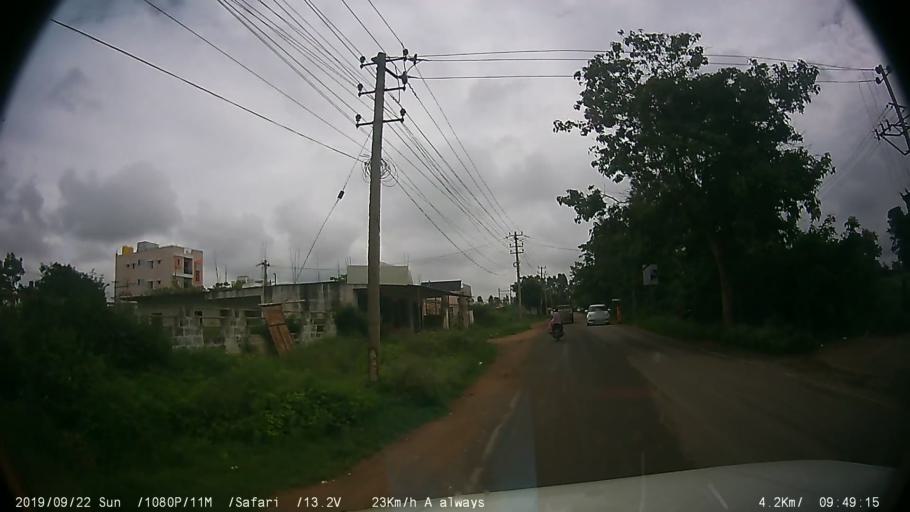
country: IN
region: Karnataka
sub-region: Bangalore Urban
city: Anekal
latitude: 12.8176
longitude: 77.6507
